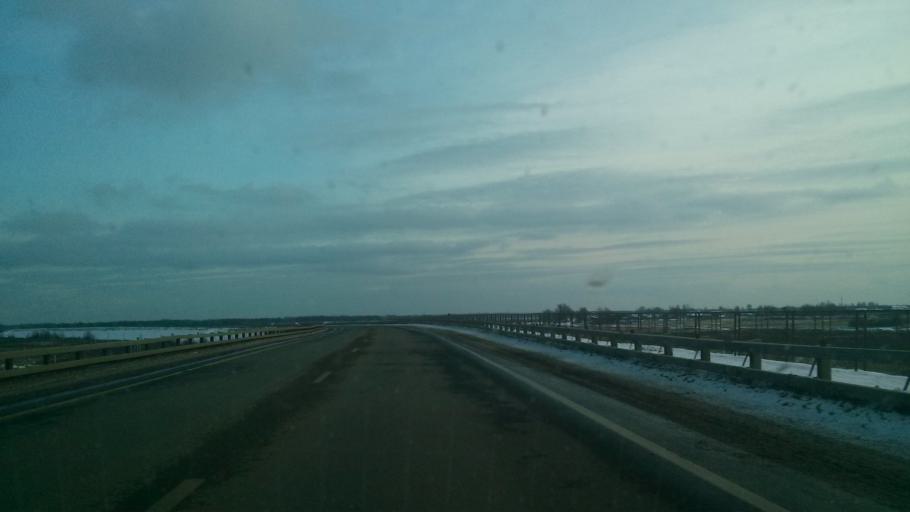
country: RU
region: Vladimir
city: Murom
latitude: 55.5901
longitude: 42.1200
